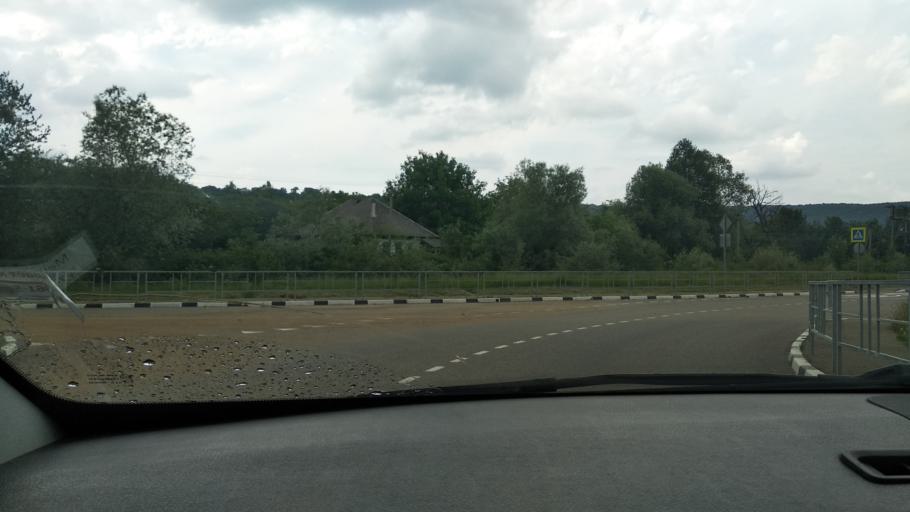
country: RU
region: Krasnodarskiy
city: Neftegorsk
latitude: 44.2717
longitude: 39.9232
